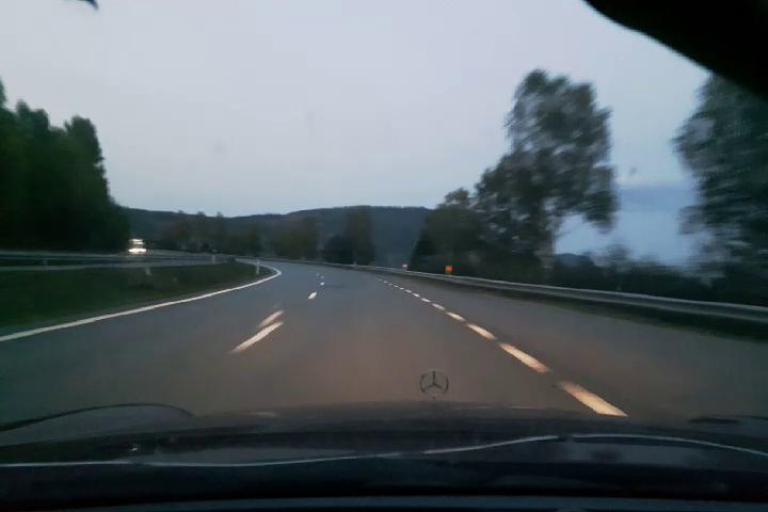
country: SE
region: Vaesternorrland
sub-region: Kramfors Kommun
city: Nordingra
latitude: 63.0105
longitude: 18.2909
